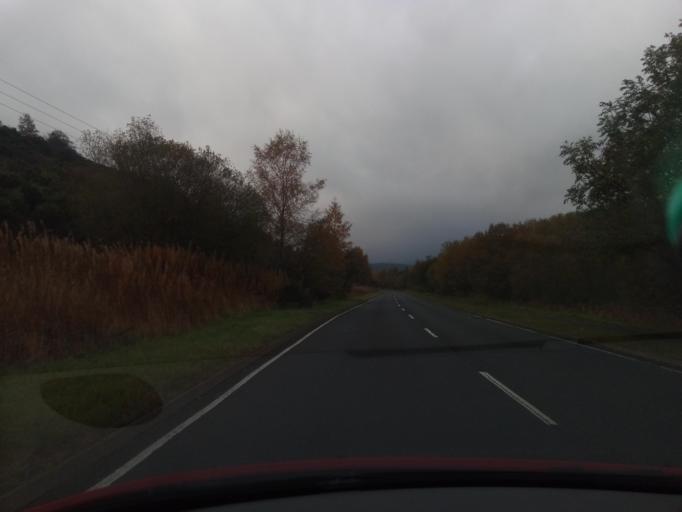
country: GB
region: Scotland
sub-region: The Scottish Borders
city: Galashiels
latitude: 55.6245
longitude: -2.8622
